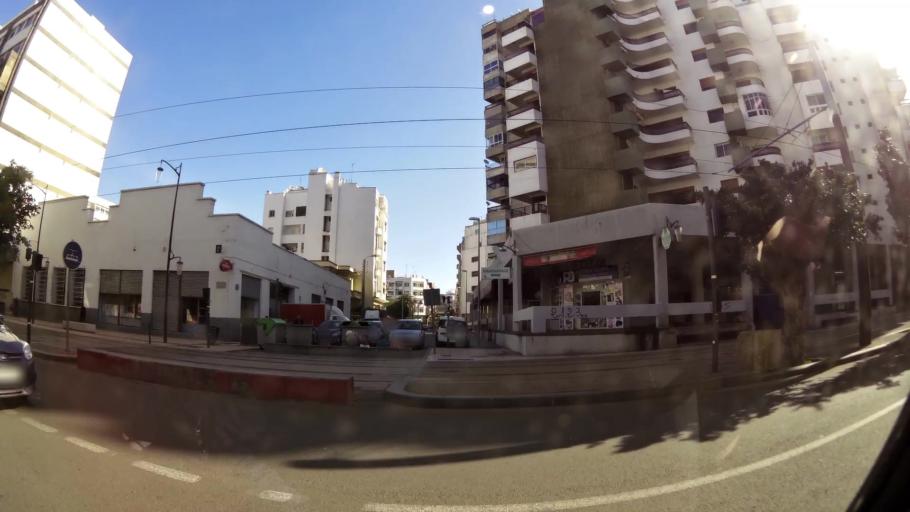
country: MA
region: Grand Casablanca
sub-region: Casablanca
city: Casablanca
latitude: 33.5910
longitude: -7.5934
